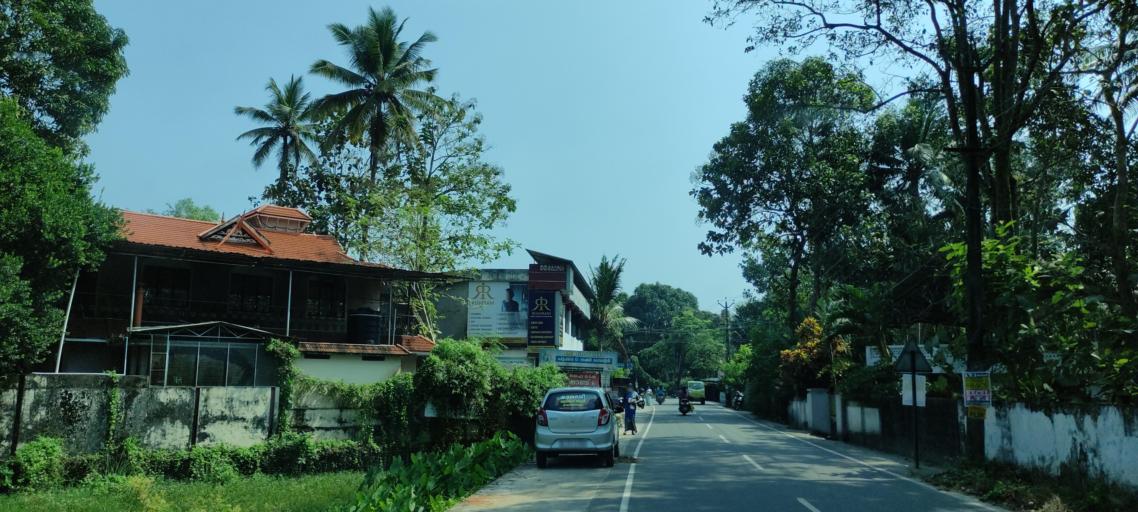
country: IN
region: Kerala
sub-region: Alappuzha
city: Shertallai
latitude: 9.6016
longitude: 76.3153
